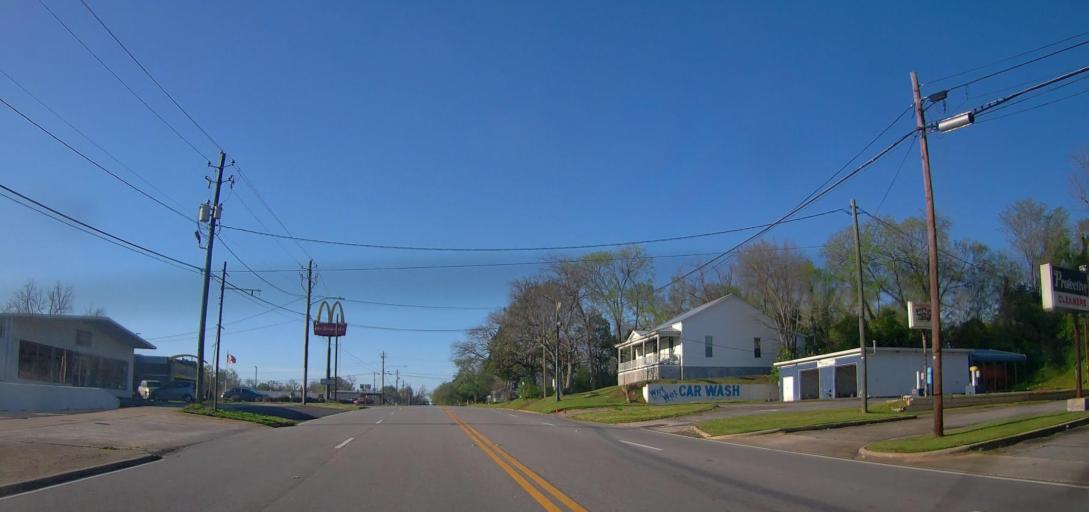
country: US
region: Georgia
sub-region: Baldwin County
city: Hardwick
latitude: 33.0730
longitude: -83.2247
